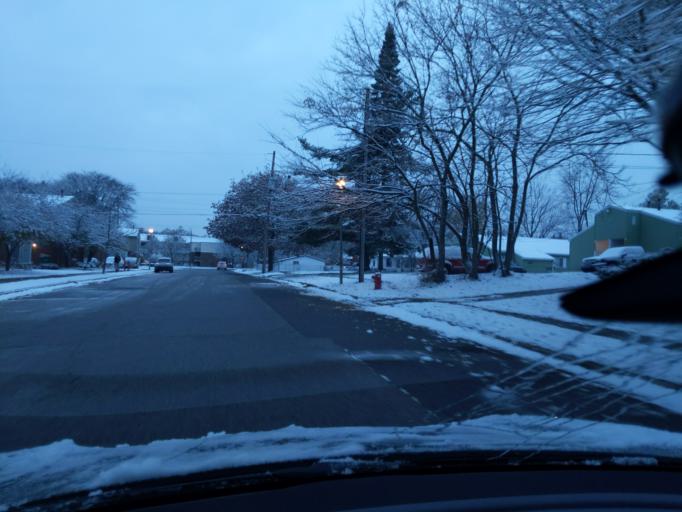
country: US
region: Michigan
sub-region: Ingham County
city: Lansing
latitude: 42.6869
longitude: -84.5660
